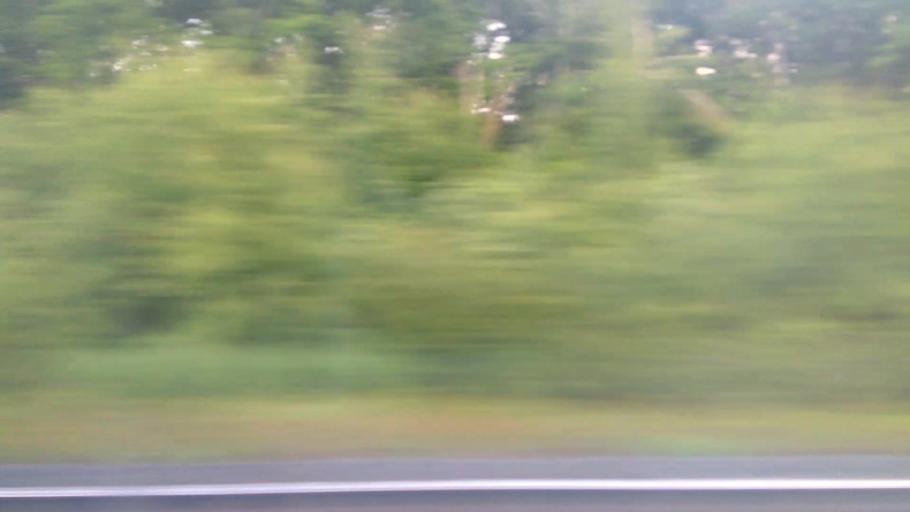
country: RU
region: Moskovskaya
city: Mikhnevo
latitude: 55.0743
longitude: 37.9799
